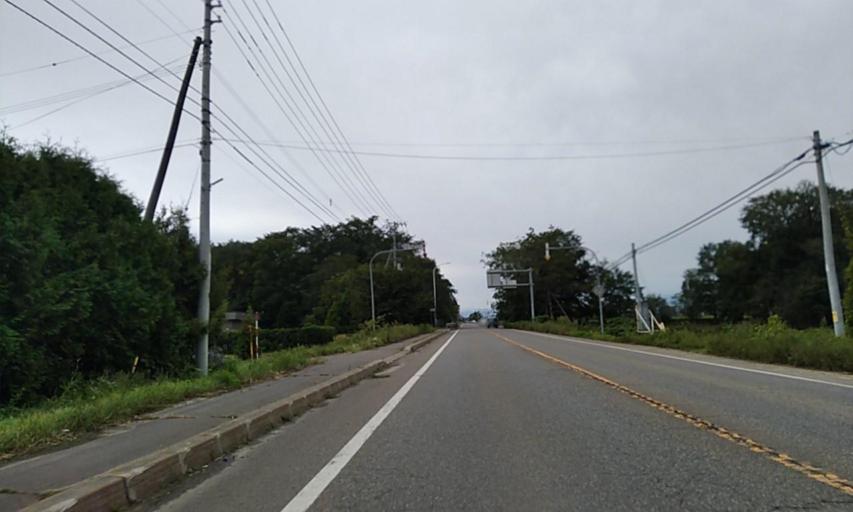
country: JP
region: Hokkaido
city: Obihiro
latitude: 42.8342
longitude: 143.1901
